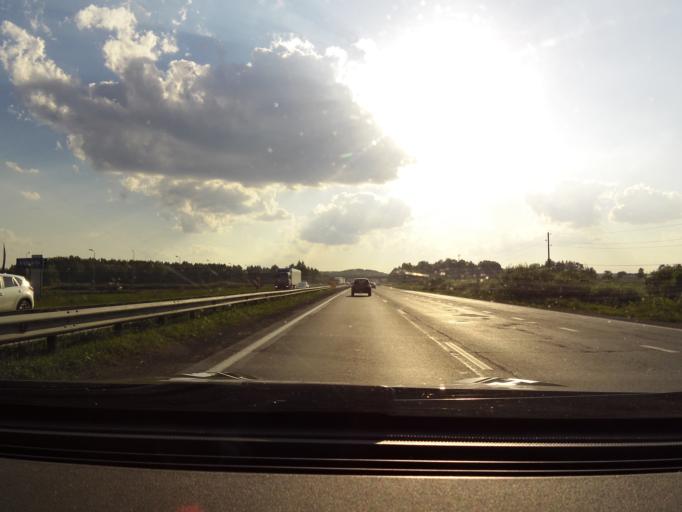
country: RU
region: Sverdlovsk
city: Talitsa
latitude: 56.8377
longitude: 60.1555
